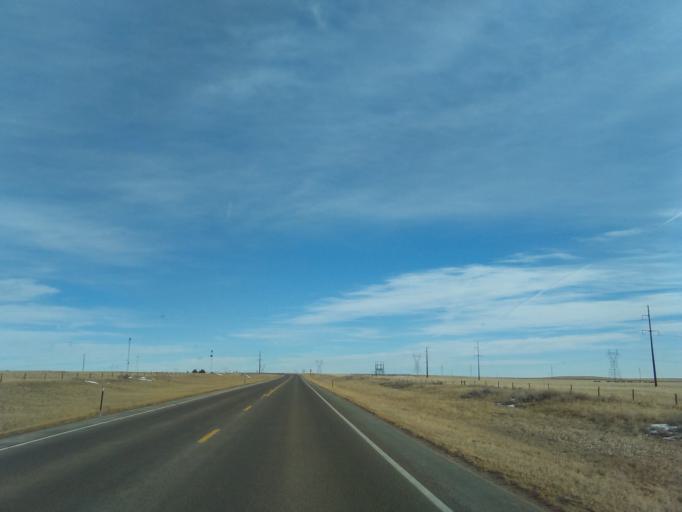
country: US
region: Wyoming
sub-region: Laramie County
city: Pine Bluffs
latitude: 41.4364
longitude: -104.3574
